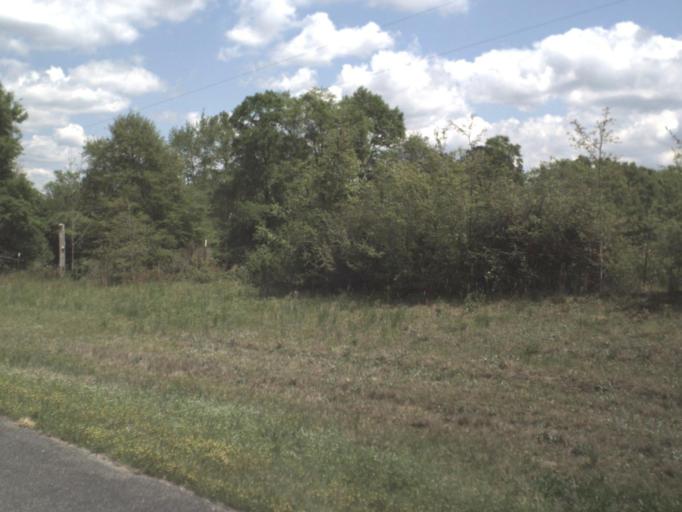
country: US
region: Florida
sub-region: Okaloosa County
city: Crestview
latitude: 30.9611
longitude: -86.6324
